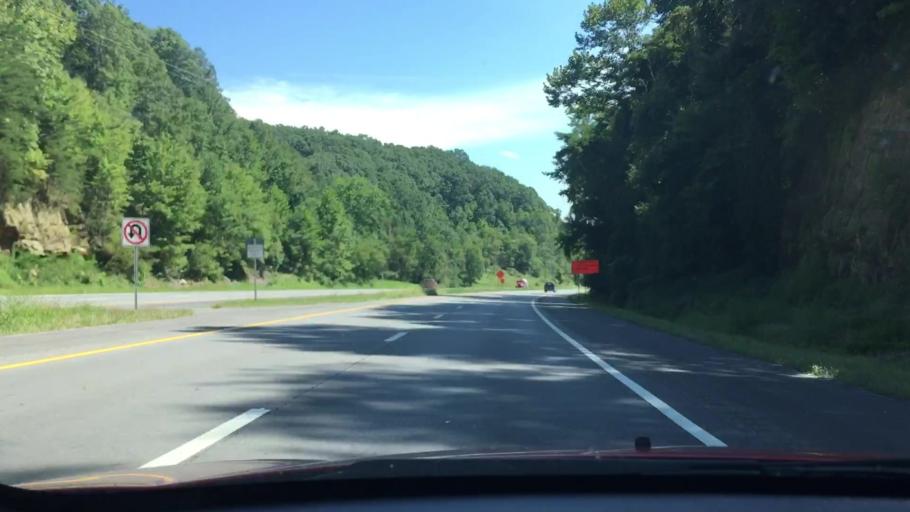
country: US
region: Ohio
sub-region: Athens County
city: Athens
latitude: 39.3470
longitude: -82.0828
